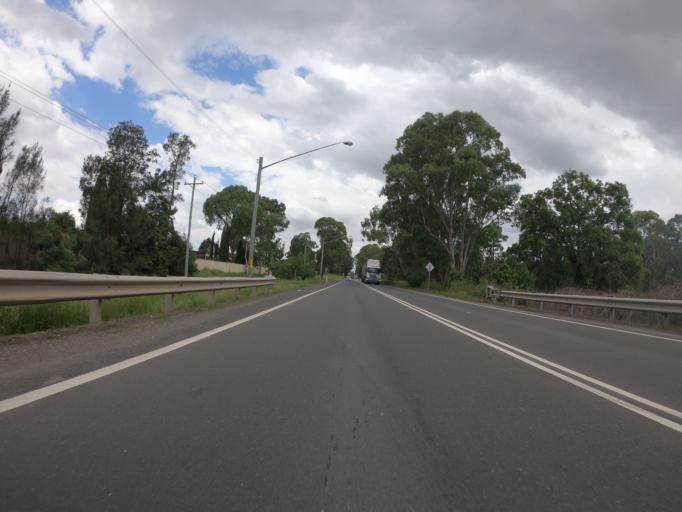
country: AU
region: New South Wales
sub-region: Blacktown
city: Mount Druitt
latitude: -33.8055
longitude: 150.7709
